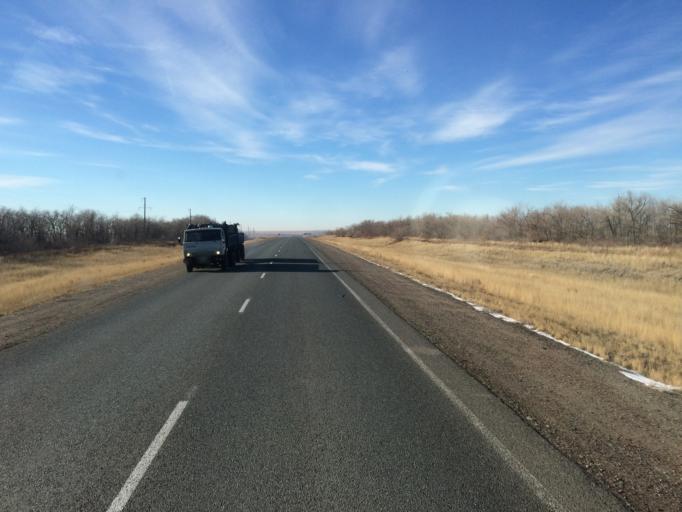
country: KZ
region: Aqtoebe
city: Aqtobe
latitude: 50.2475
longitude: 56.7959
